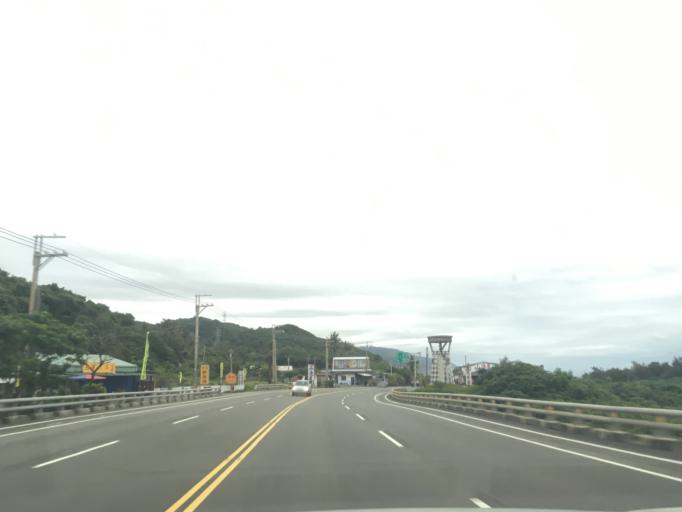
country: TW
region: Taiwan
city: Hengchun
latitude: 22.3024
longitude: 120.8889
